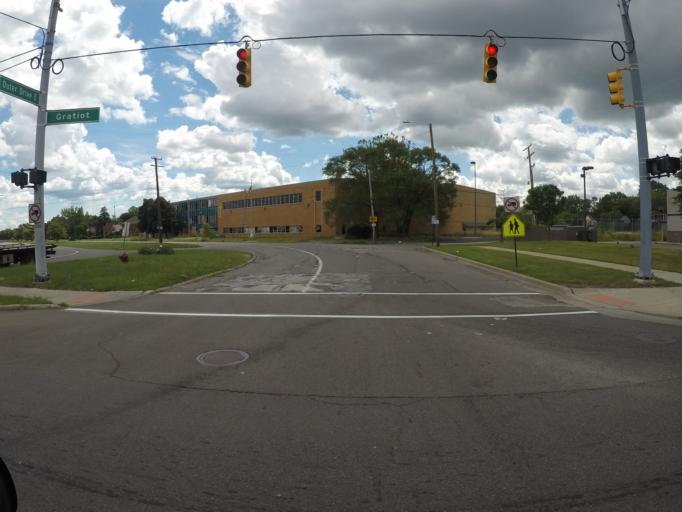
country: US
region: Michigan
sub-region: Wayne County
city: Hamtramck
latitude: 42.4063
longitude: -82.9964
